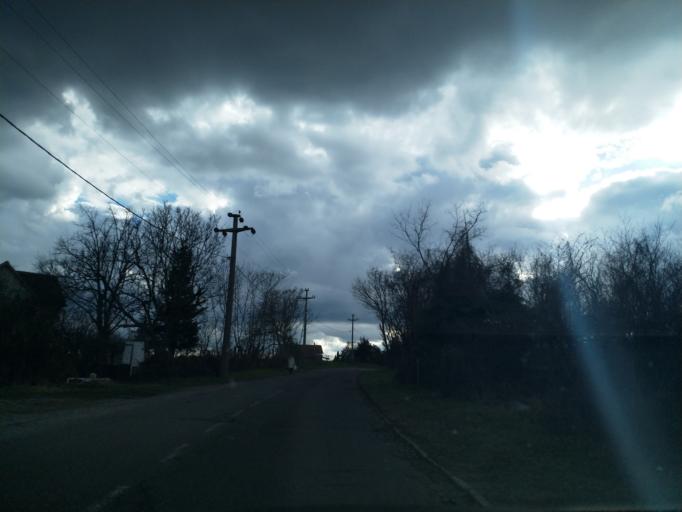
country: RS
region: Central Serbia
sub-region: Belgrade
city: Grocka
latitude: 44.6217
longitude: 20.7421
